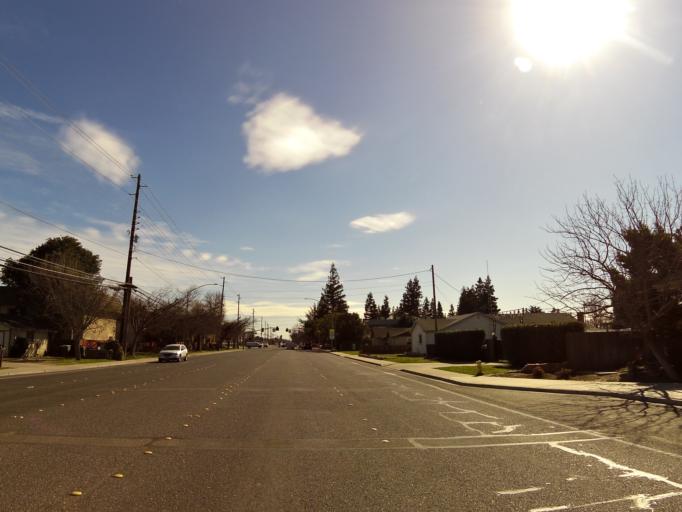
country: US
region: California
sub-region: Stanislaus County
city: Modesto
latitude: 37.6833
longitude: -120.9760
